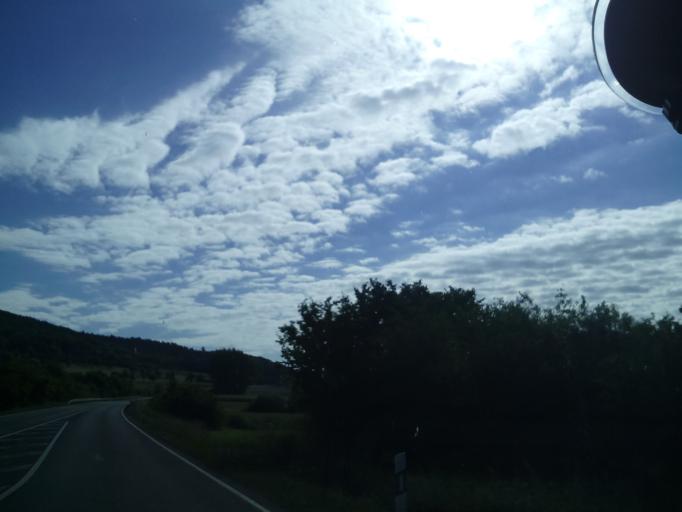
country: DE
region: Bavaria
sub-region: Upper Franconia
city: Eggolsheim
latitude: 49.8060
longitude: 11.0820
